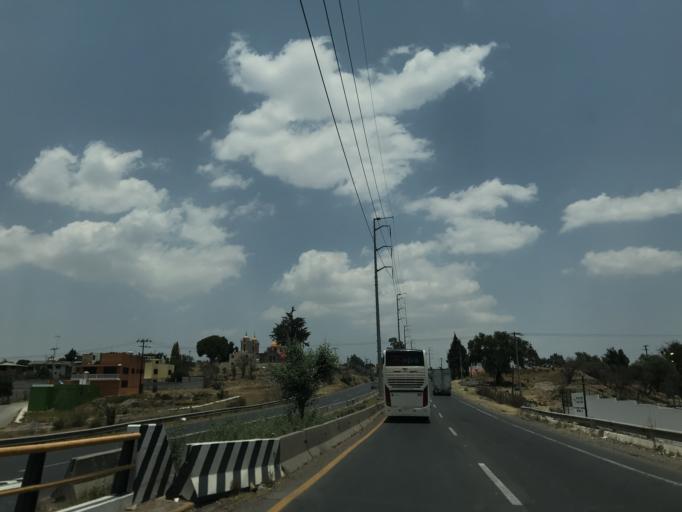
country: MX
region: Tlaxcala
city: Yauhquemehcan
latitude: 19.4047
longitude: -98.1714
